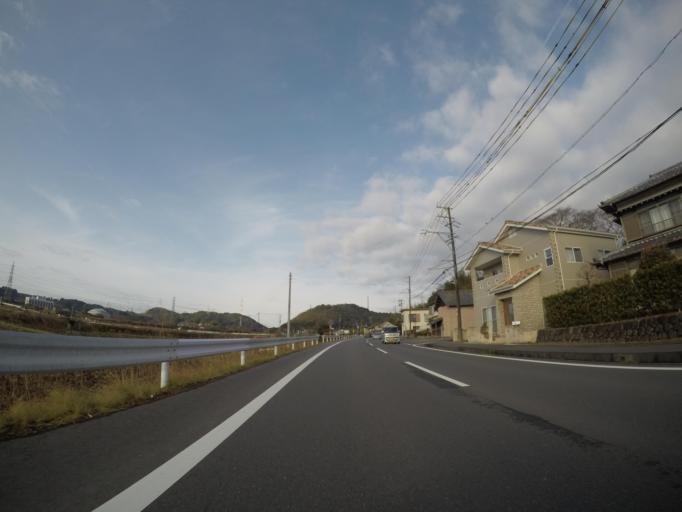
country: JP
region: Shizuoka
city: Hamakita
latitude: 34.8208
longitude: 137.7114
